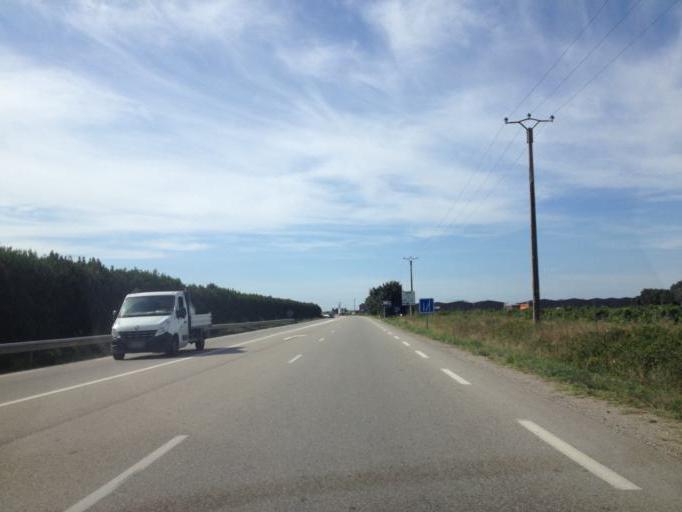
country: FR
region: Provence-Alpes-Cote d'Azur
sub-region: Departement du Vaucluse
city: Courthezon
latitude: 44.1053
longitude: 4.8575
